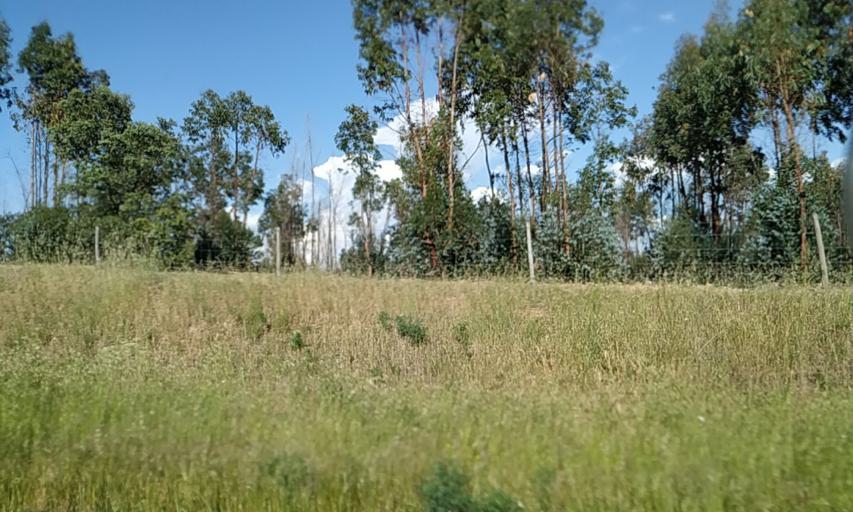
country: PT
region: Portalegre
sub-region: Fronteira
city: Fronteira
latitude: 39.0036
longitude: -7.4678
